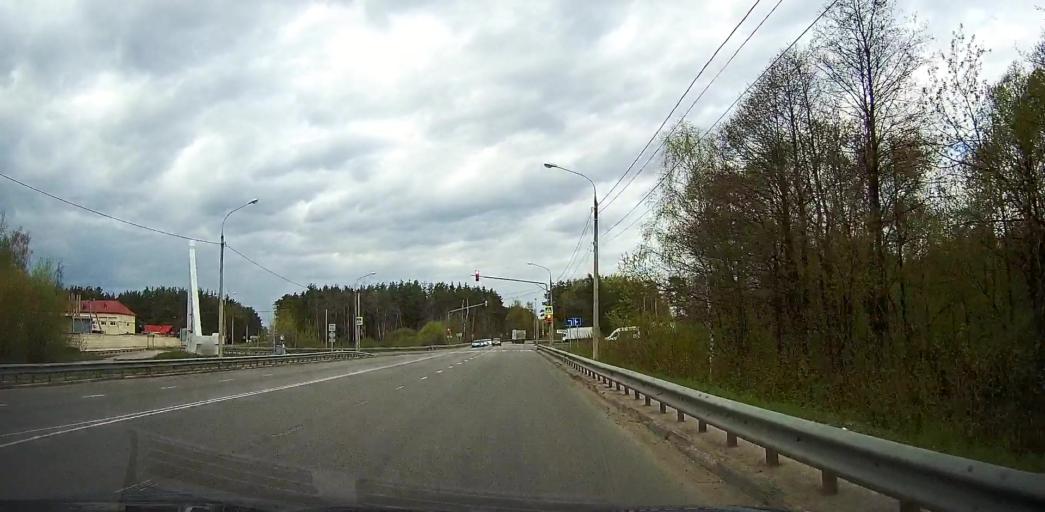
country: RU
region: Moskovskaya
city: Pavlovskiy Posad
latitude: 55.7999
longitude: 38.6523
